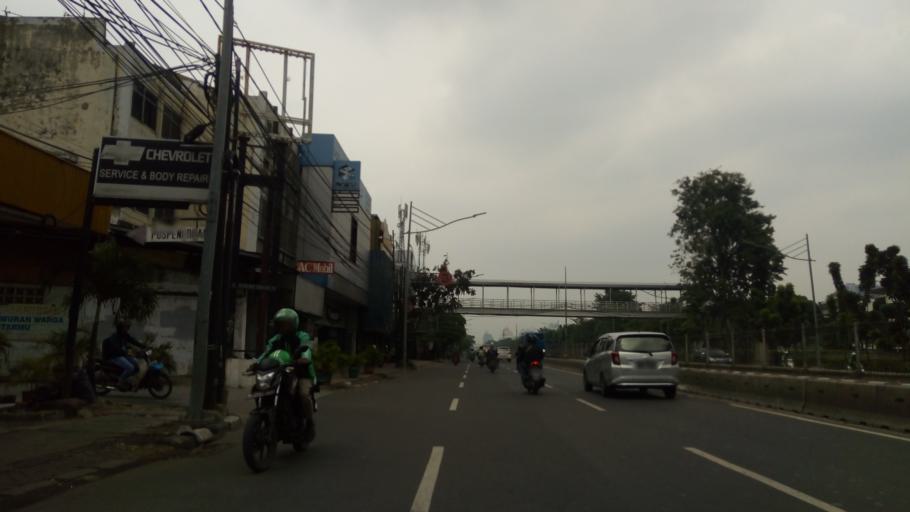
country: ID
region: Jakarta Raya
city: Jakarta
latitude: -6.1510
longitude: 106.8354
